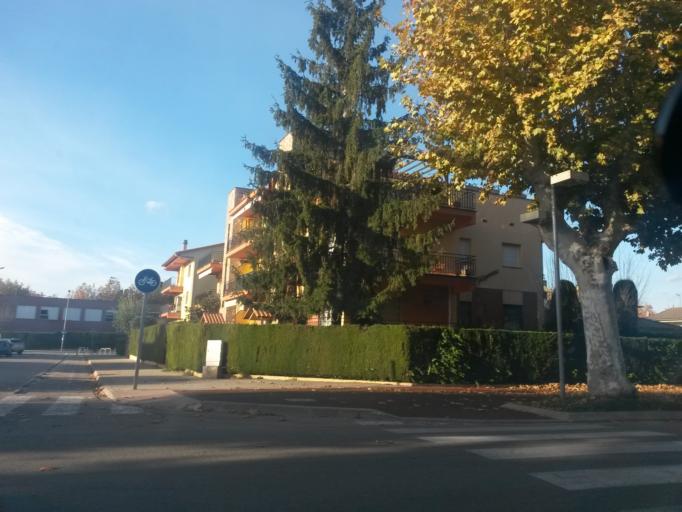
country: ES
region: Catalonia
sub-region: Provincia de Girona
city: Banyoles
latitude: 42.1143
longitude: 2.7552
